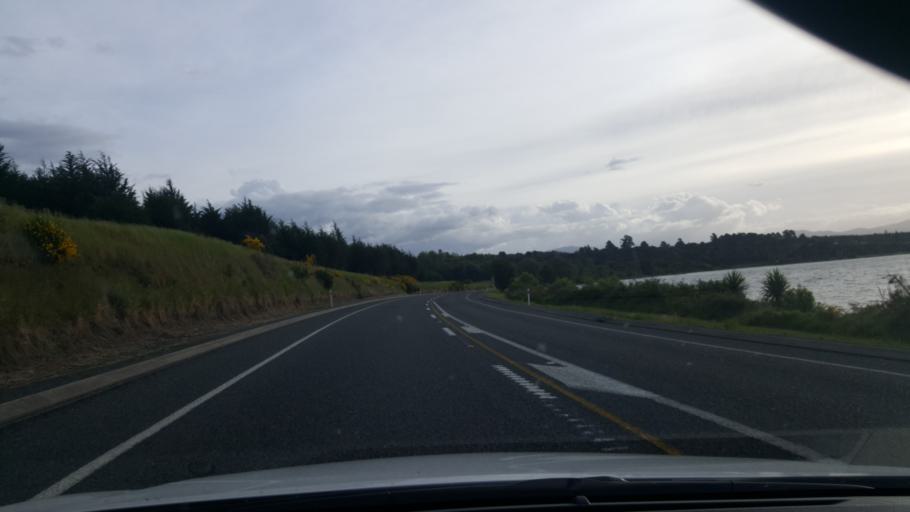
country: NZ
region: Waikato
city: Turangi
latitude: -38.9013
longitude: 175.9439
